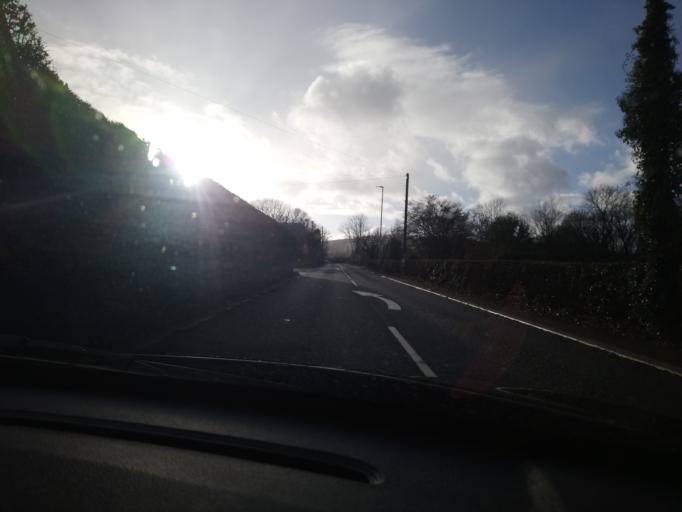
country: GB
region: Wales
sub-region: Wrexham
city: Chirk
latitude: 52.9603
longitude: -3.0622
